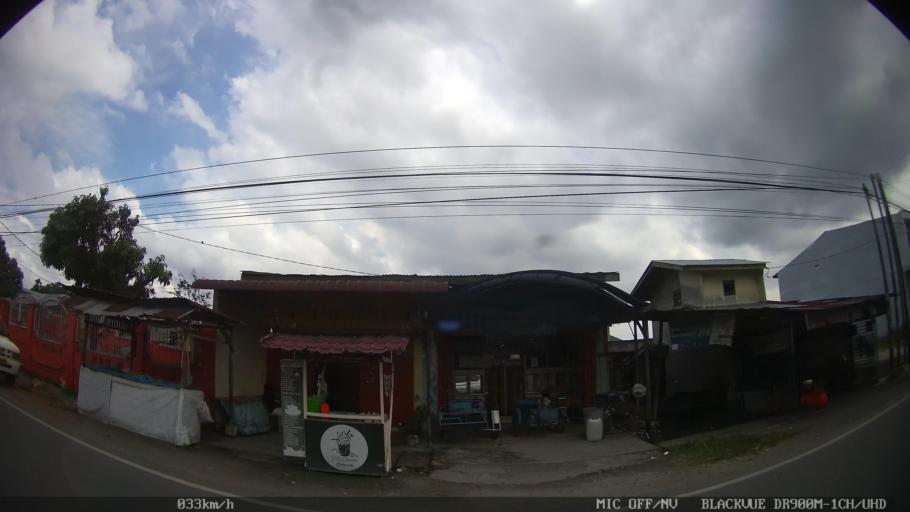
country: ID
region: North Sumatra
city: Sunggal
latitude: 3.6183
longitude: 98.6159
